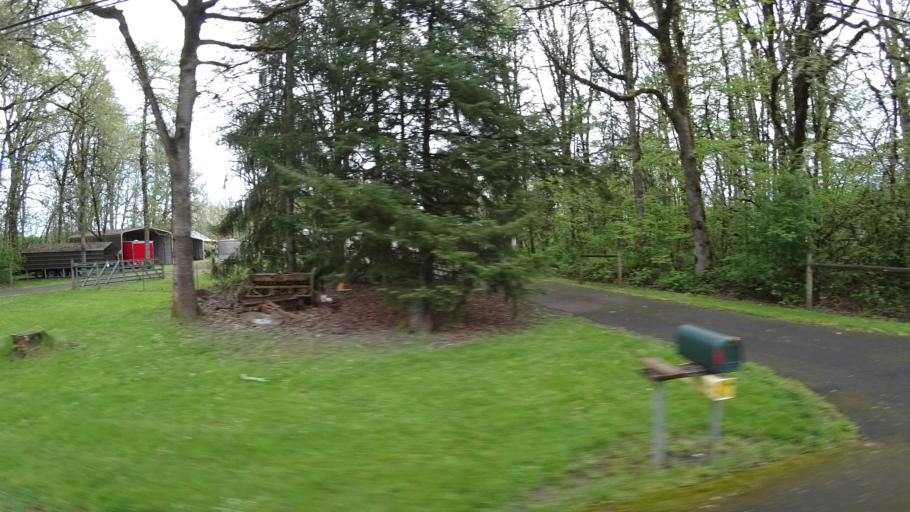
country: US
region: Oregon
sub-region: Washington County
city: Hillsboro
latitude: 45.5562
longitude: -122.9584
